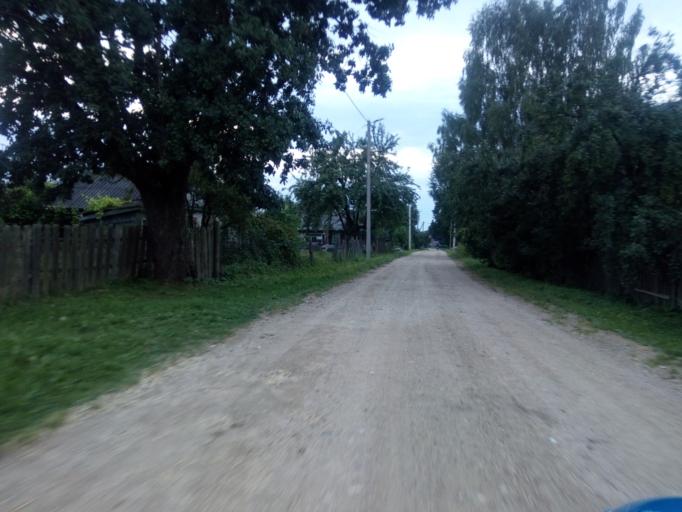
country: BY
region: Vitebsk
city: Dzisna
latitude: 55.6692
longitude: 28.3225
